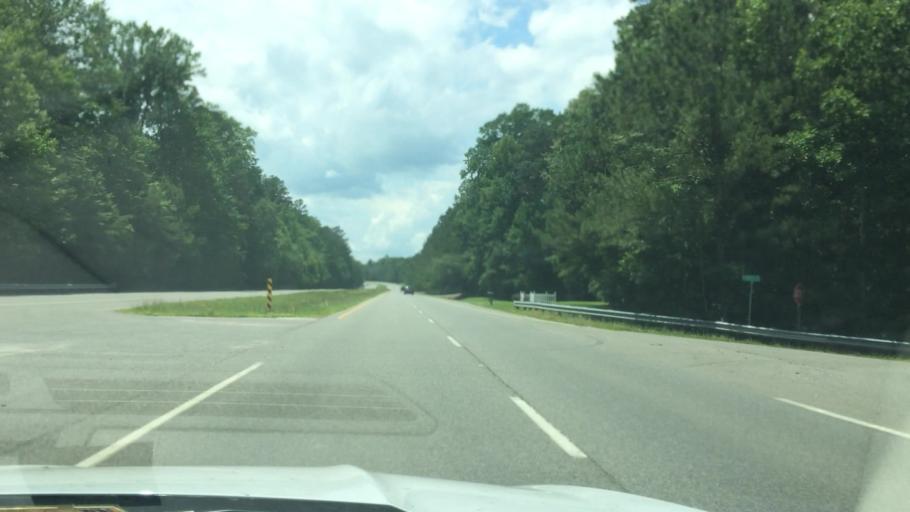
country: US
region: Virginia
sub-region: Middlesex County
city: Saluda
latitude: 37.5641
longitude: -76.6399
